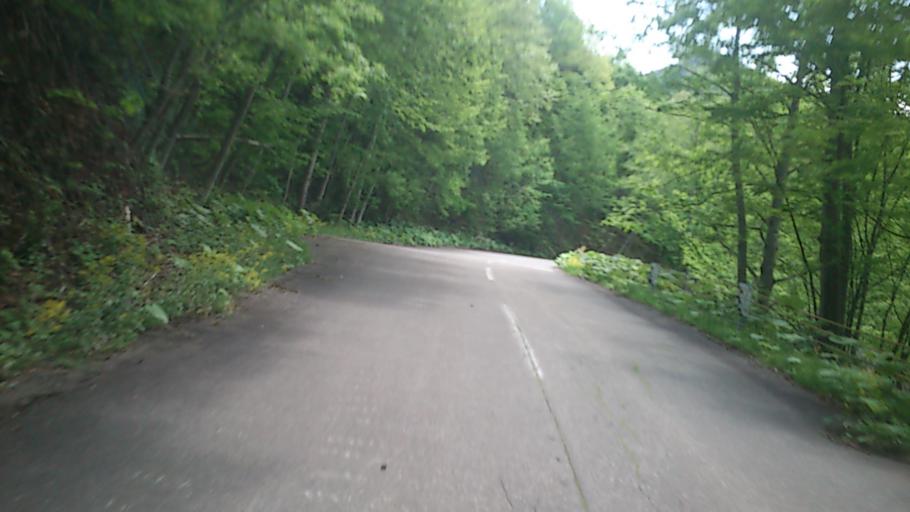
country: JP
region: Hokkaido
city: Otofuke
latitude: 43.3718
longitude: 143.2173
